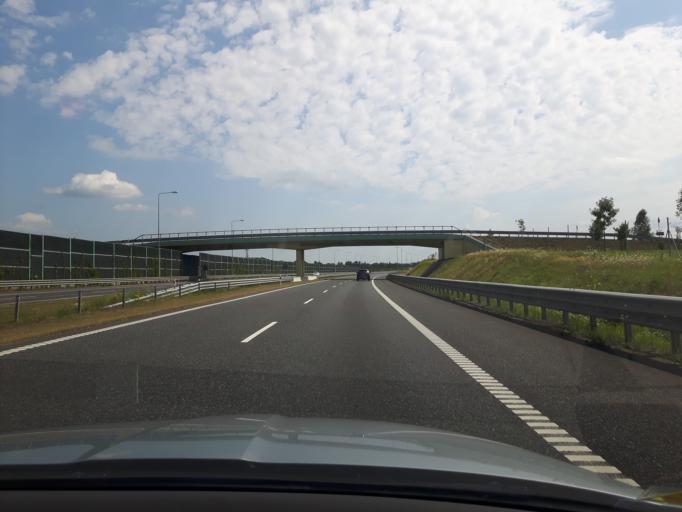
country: PL
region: Warmian-Masurian Voivodeship
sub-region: Powiat olsztynski
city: Olsztynek
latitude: 53.5864
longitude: 20.2436
